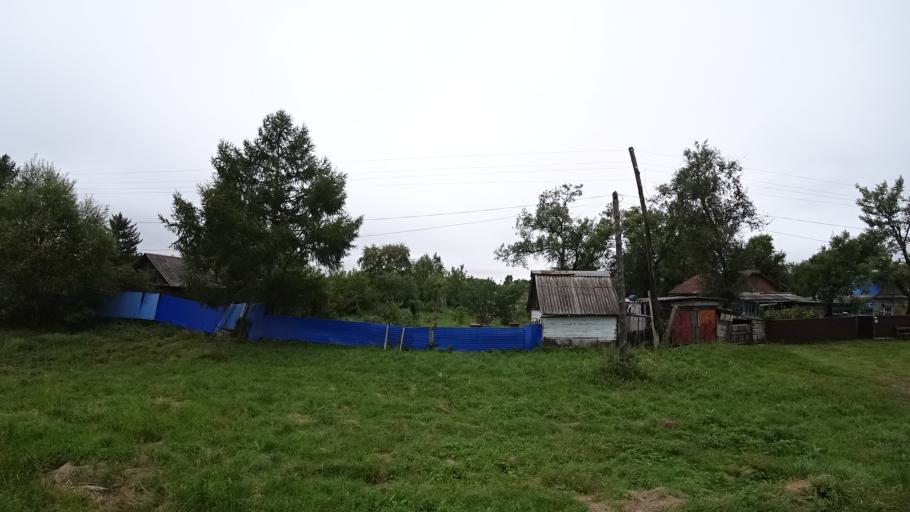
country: RU
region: Primorskiy
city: Monastyrishche
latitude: 44.0897
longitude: 132.5783
